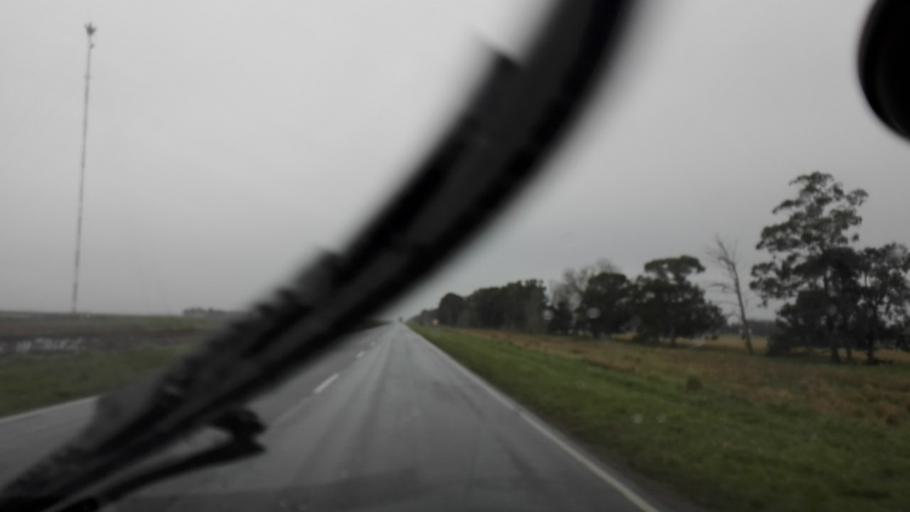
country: AR
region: Buenos Aires
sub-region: Partido de Tandil
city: Tandil
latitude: -37.0920
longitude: -58.9989
